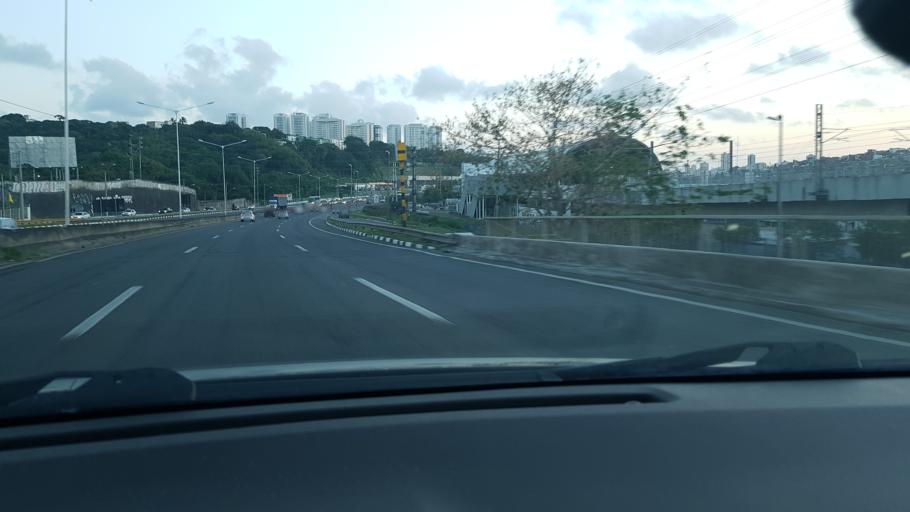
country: BR
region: Bahia
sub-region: Salvador
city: Salvador
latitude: -12.9543
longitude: -38.4713
